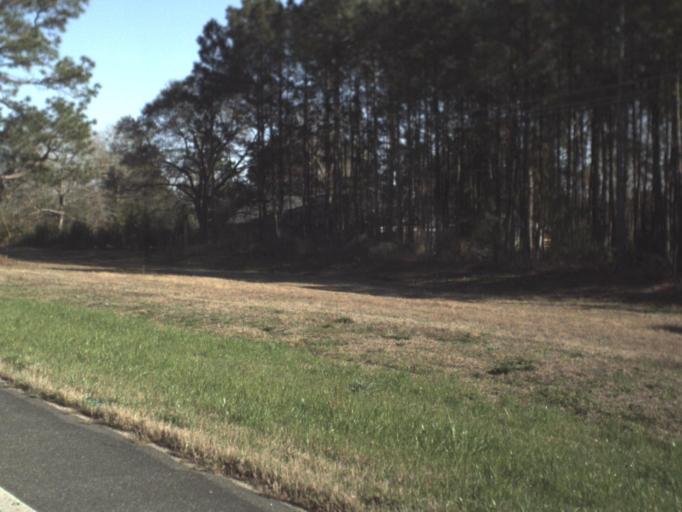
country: US
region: Florida
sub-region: Jackson County
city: Marianna
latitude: 30.7847
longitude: -85.3104
